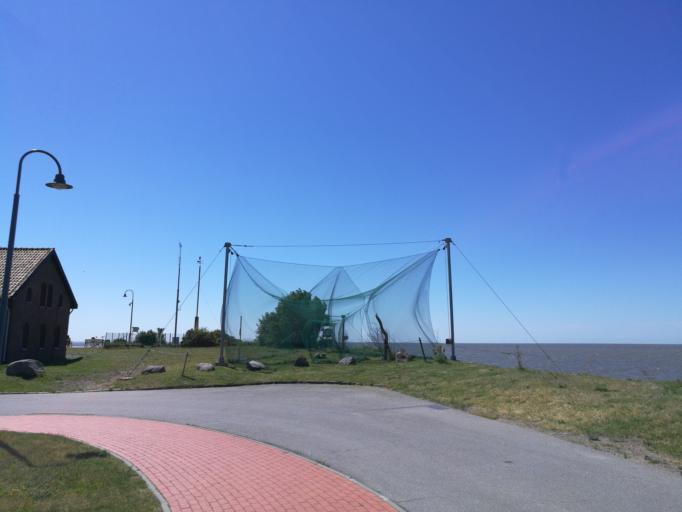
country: LT
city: Neringa
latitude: 55.3414
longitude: 21.1897
